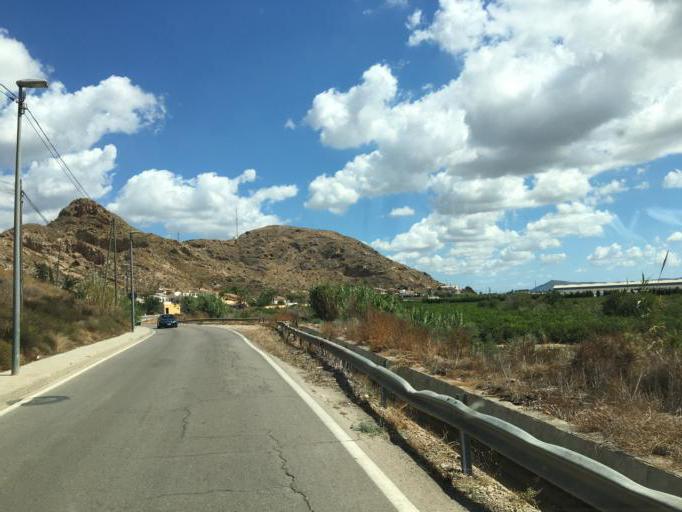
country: ES
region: Murcia
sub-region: Murcia
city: Santomera
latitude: 38.0514
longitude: -1.0653
